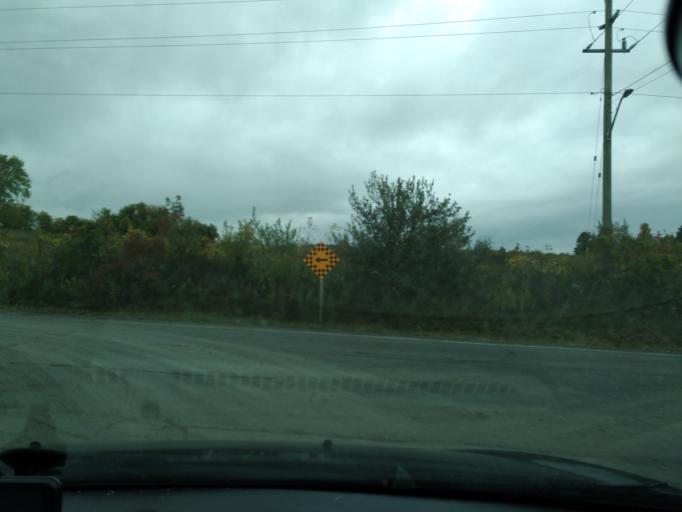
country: CA
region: Ontario
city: Bradford West Gwillimbury
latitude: 44.1421
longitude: -79.5568
